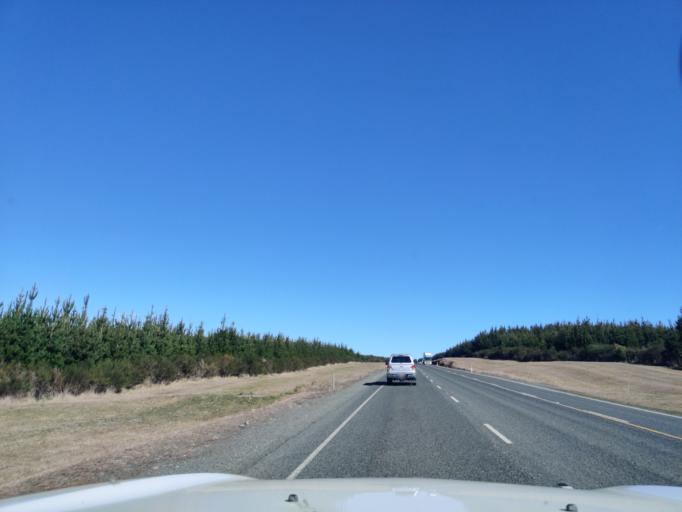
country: NZ
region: Waikato
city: Turangi
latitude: -39.1235
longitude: 175.7963
